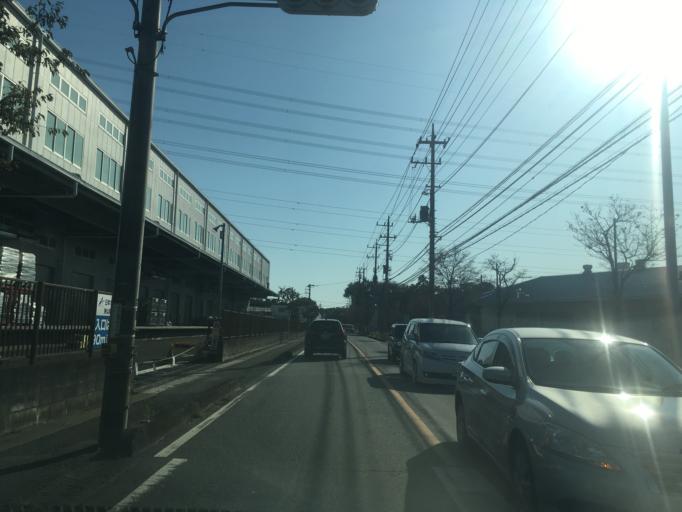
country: JP
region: Saitama
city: Tokorozawa
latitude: 35.8430
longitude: 139.4667
